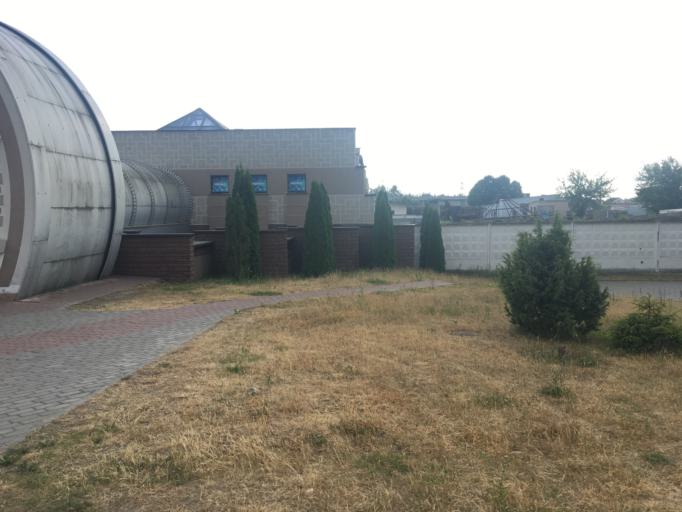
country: BY
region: Grodnenskaya
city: Hrodna
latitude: 53.6543
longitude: 23.8308
